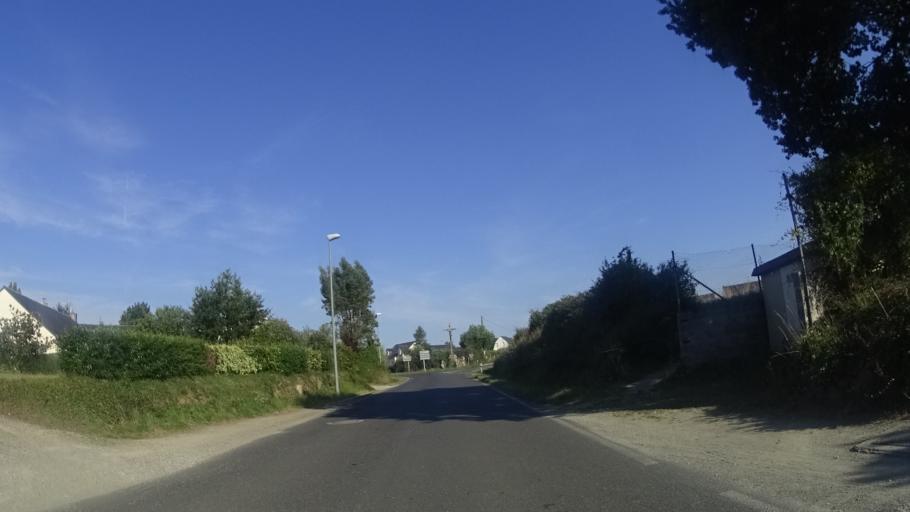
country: FR
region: Pays de la Loire
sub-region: Departement de la Loire-Atlantique
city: Joue-sur-Erdre
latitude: 47.4976
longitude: -1.4247
